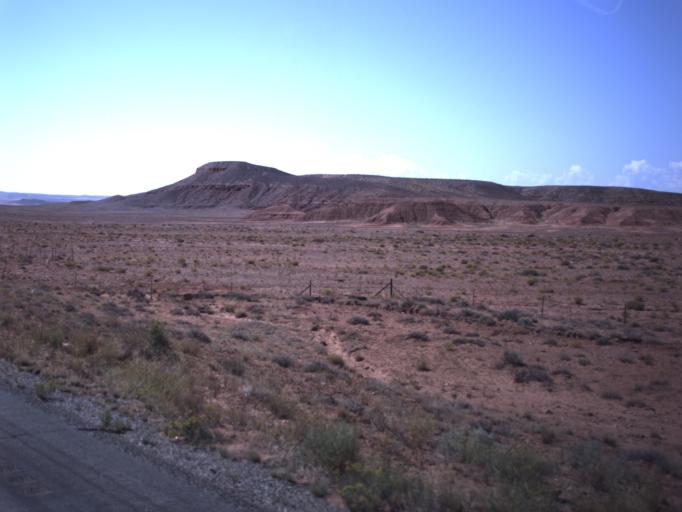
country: US
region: Utah
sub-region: San Juan County
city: Blanding
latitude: 37.0071
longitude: -109.6113
